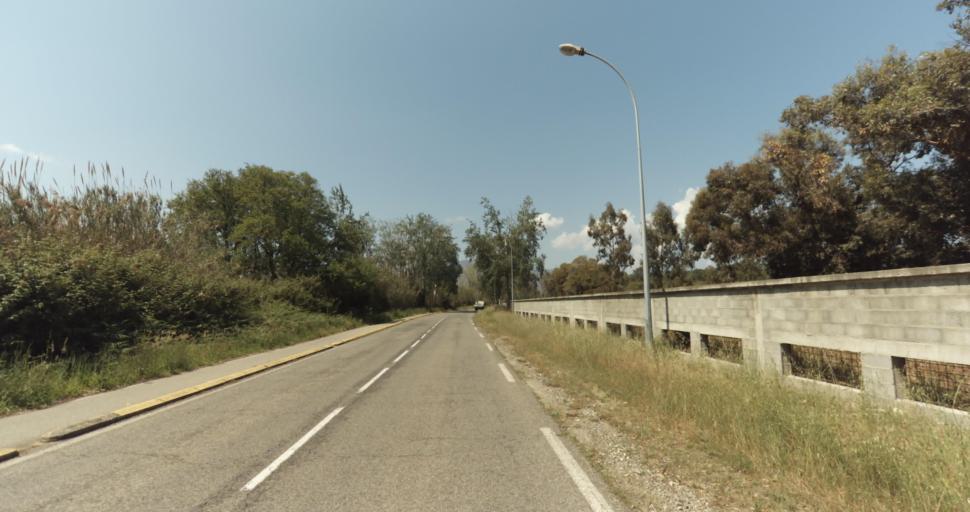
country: FR
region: Corsica
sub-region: Departement de la Haute-Corse
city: Biguglia
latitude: 42.6245
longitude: 9.4704
